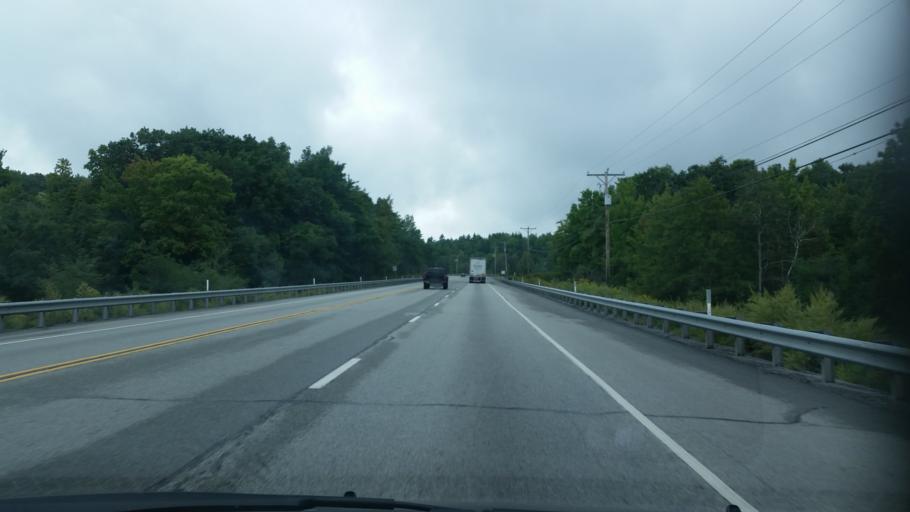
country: US
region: Pennsylvania
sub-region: Clearfield County
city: Shiloh
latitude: 41.0166
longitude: -78.3475
